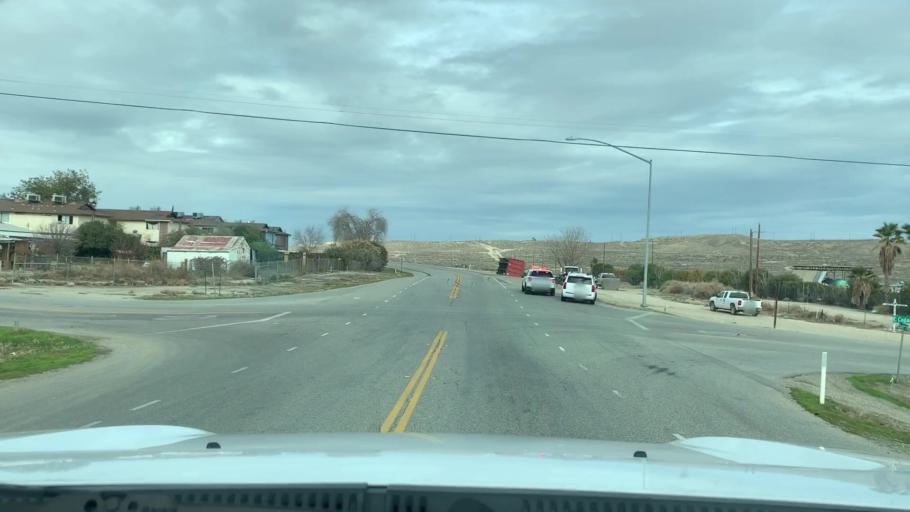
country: US
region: California
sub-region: Kern County
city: Ford City
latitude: 35.1544
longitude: -119.4479
